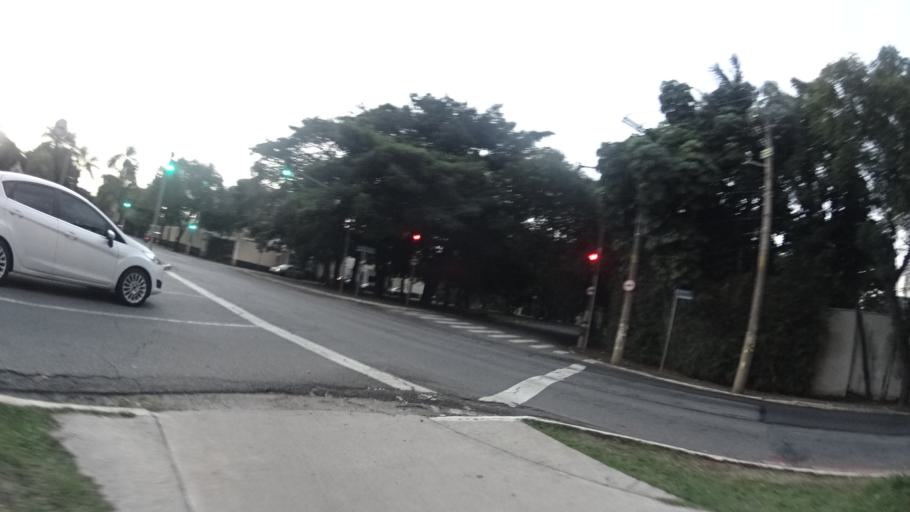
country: BR
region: Sao Paulo
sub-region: Sao Paulo
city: Sao Paulo
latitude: -23.5510
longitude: -46.7119
